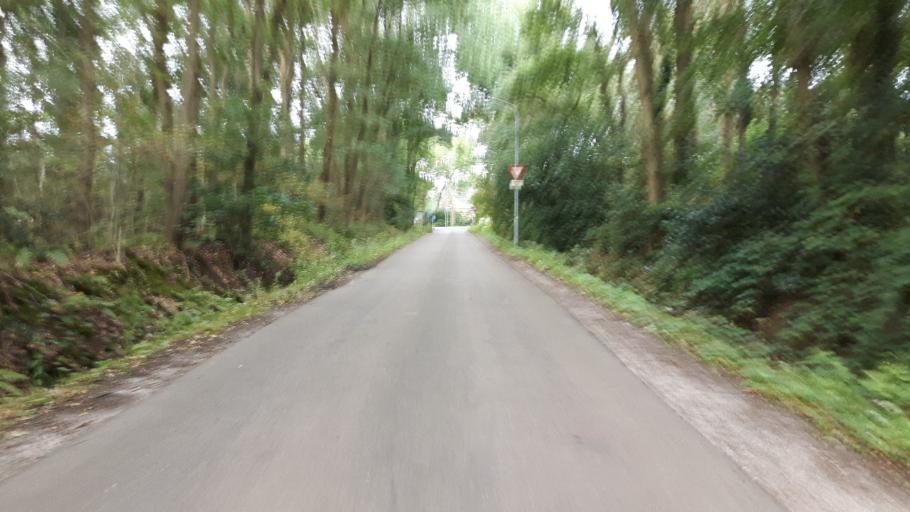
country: NL
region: Groningen
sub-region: Gemeente Leek
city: Leek
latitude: 53.1126
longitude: 6.4281
